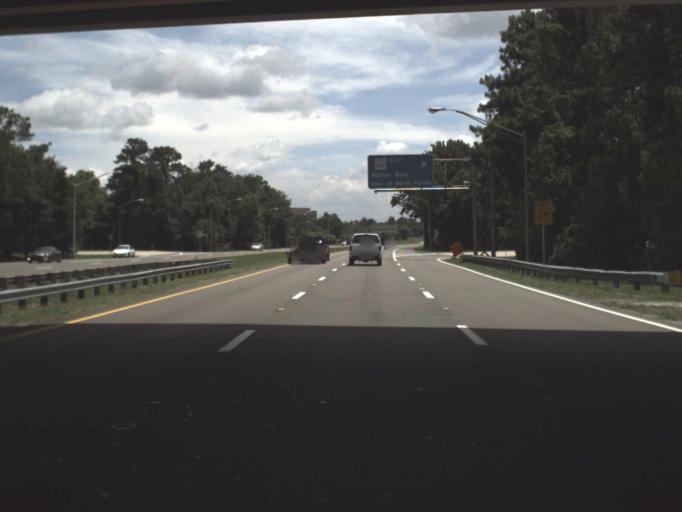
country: US
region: Florida
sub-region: Duval County
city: Jacksonville
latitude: 30.2500
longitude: -81.5526
